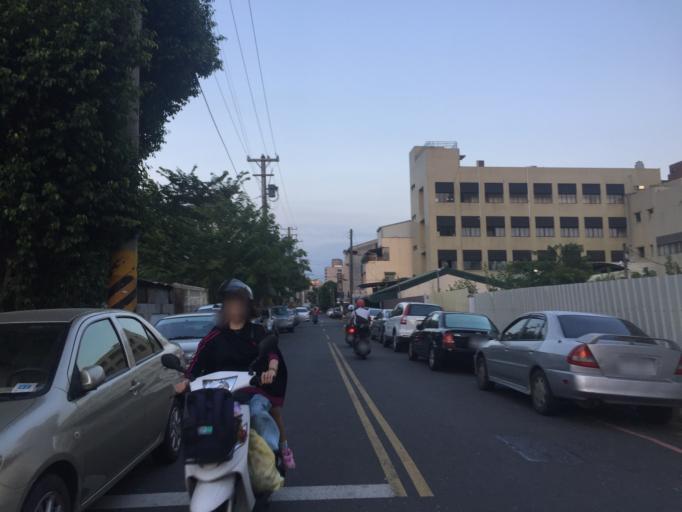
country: TW
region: Taiwan
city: Xinying
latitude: 23.3054
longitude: 120.3172
